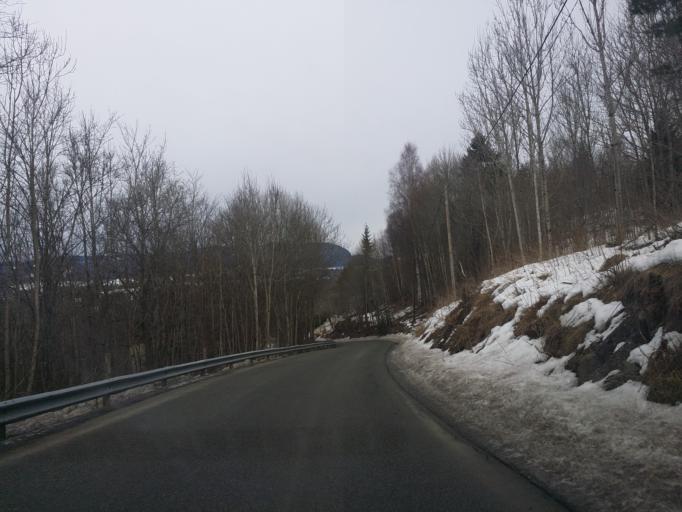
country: NO
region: Buskerud
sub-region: Lier
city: Tranby
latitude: 59.8512
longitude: 10.2723
